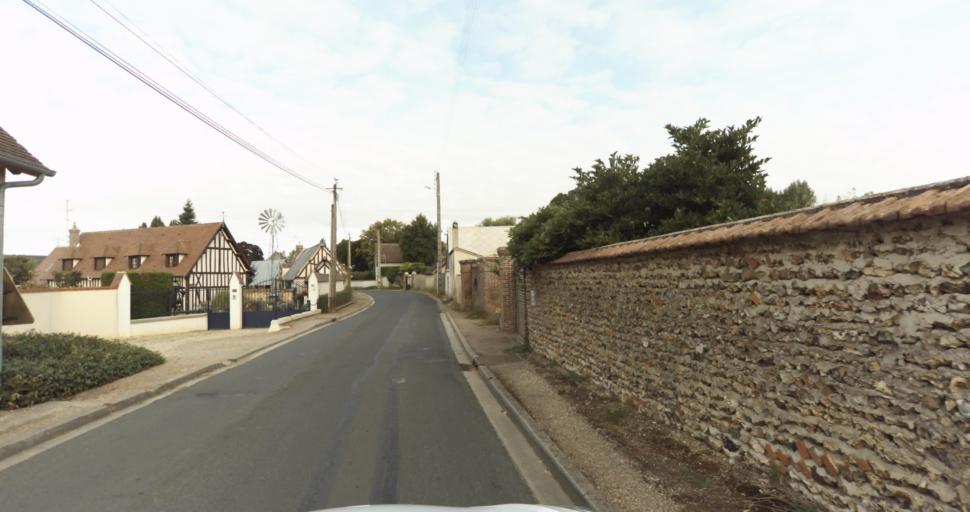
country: FR
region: Haute-Normandie
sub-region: Departement de l'Eure
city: Saint-Germain-sur-Avre
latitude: 48.8185
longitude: 1.2822
